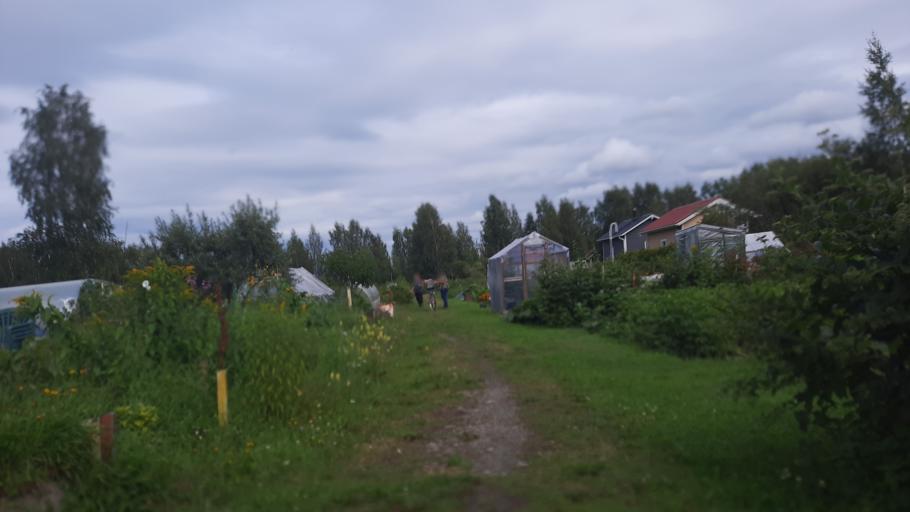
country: FI
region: North Karelia
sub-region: Joensuu
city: Joensuu
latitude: 62.6148
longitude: 29.8489
